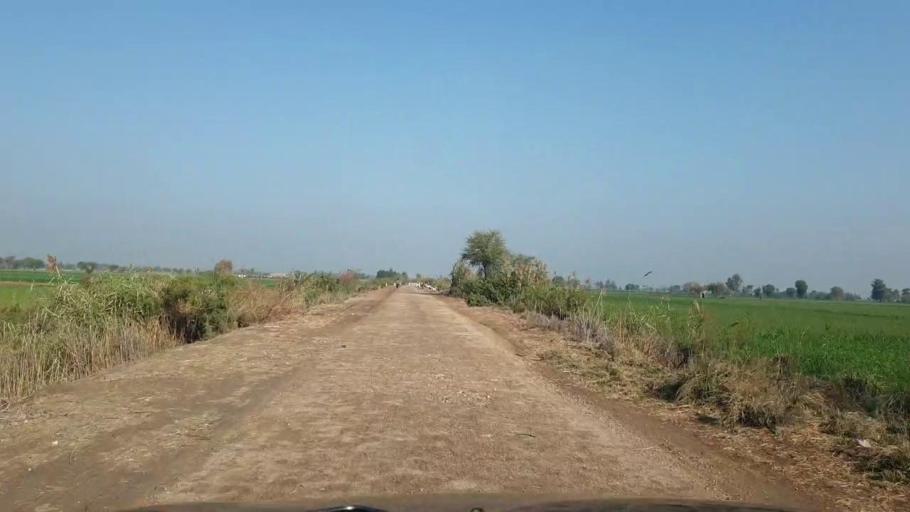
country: PK
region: Sindh
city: Sinjhoro
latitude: 26.0576
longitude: 68.7882
